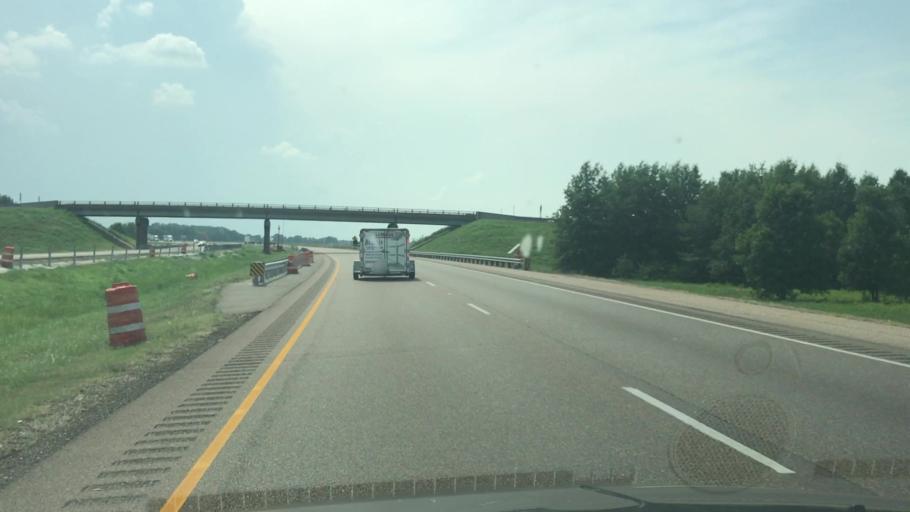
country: US
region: Arkansas
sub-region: Crittenden County
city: Earle
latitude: 35.1513
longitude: -90.3990
